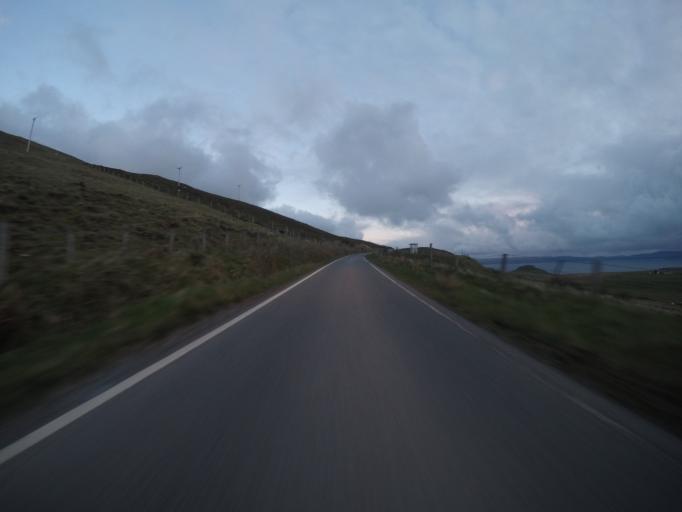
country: GB
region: Scotland
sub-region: Highland
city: Portree
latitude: 57.6082
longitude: -6.3740
